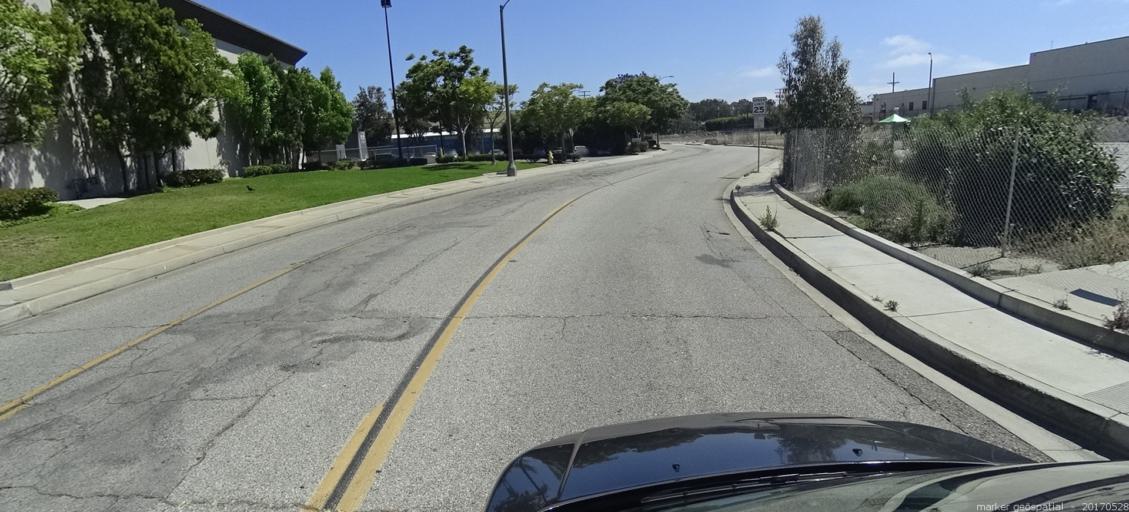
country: US
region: California
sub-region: Los Angeles County
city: Lawndale
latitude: 33.8683
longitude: -118.3563
